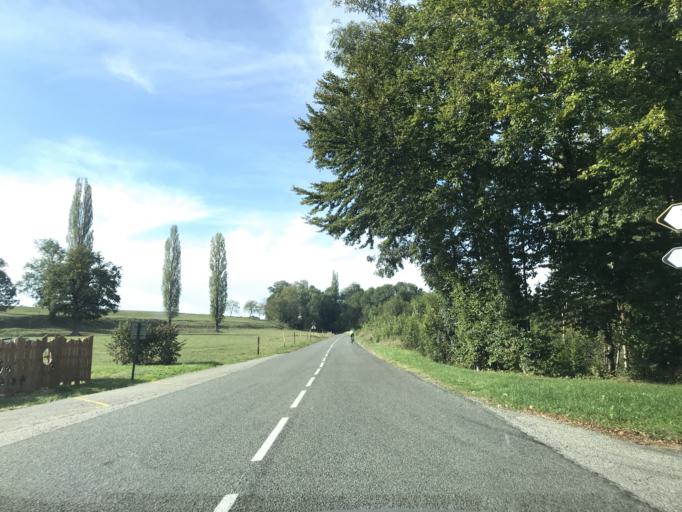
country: FR
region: Rhone-Alpes
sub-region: Departement de la Savoie
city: Yenne
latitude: 45.6806
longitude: 5.7902
